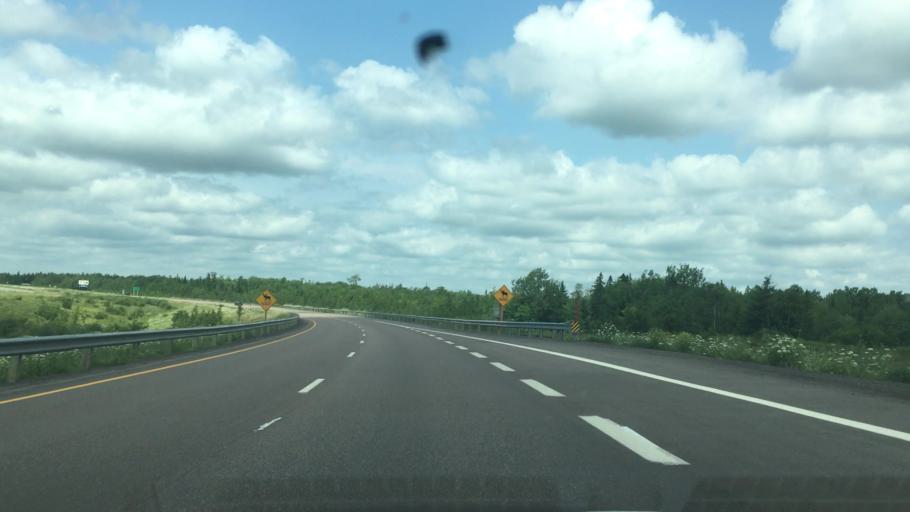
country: CA
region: New Brunswick
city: Dieppe
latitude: 46.1067
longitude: -64.6085
